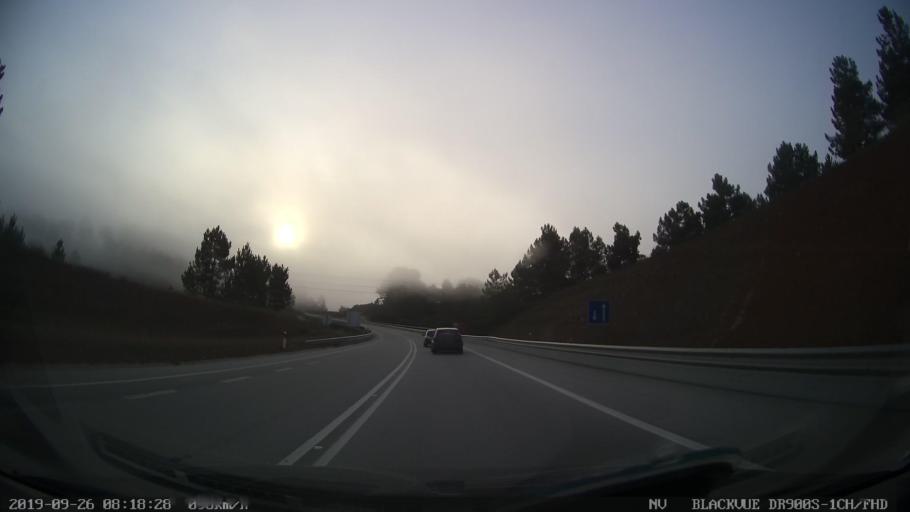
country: PT
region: Vila Real
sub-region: Vila Real
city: Vila Real
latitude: 41.2640
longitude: -7.6735
